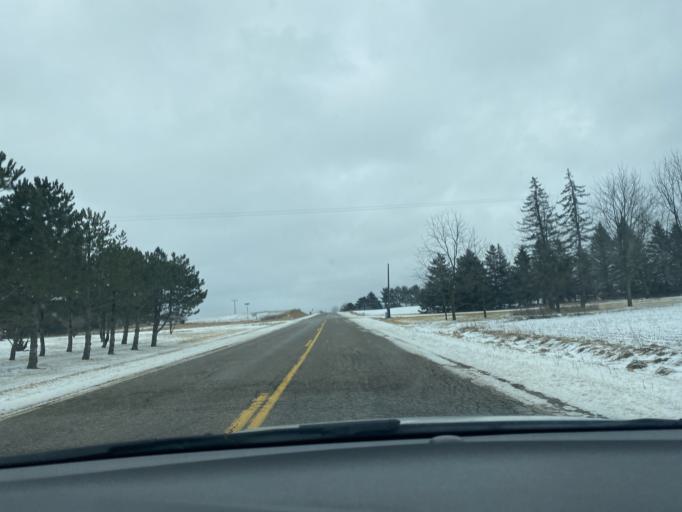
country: US
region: Michigan
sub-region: Lapeer County
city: North Branch
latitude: 43.2091
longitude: -83.1373
